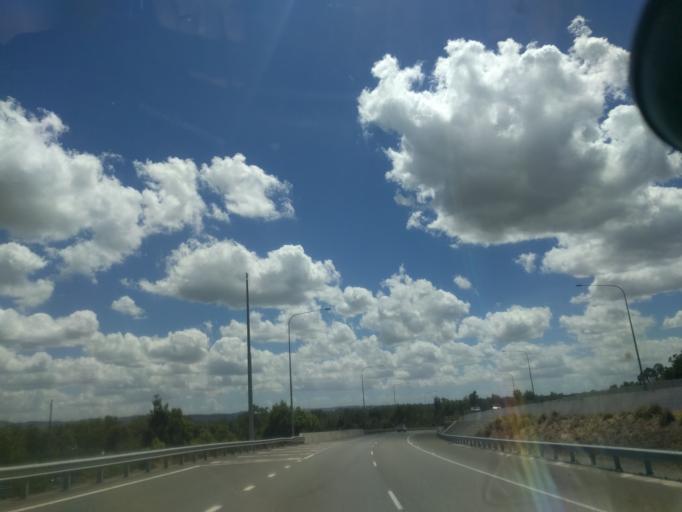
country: AU
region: Queensland
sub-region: Ipswich
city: Riverview
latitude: -27.5975
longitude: 152.8350
